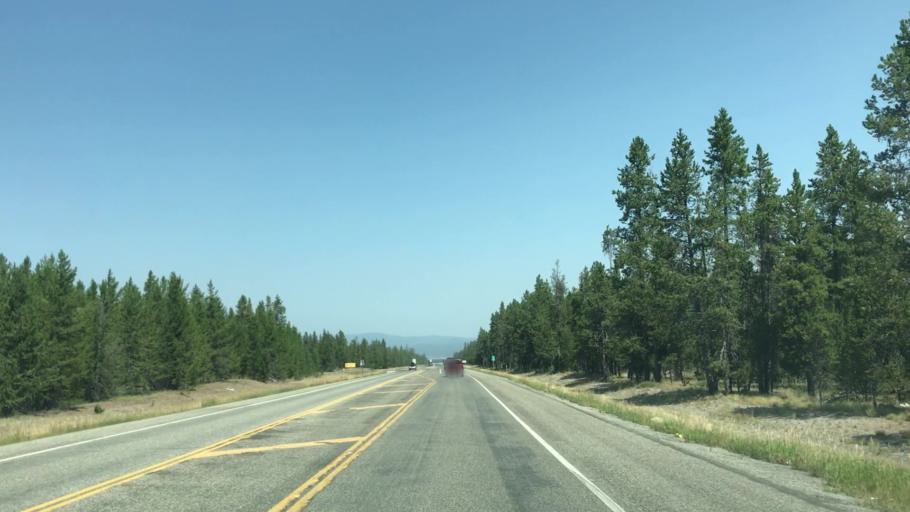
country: US
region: Montana
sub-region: Gallatin County
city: West Yellowstone
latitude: 44.6850
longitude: -111.1010
